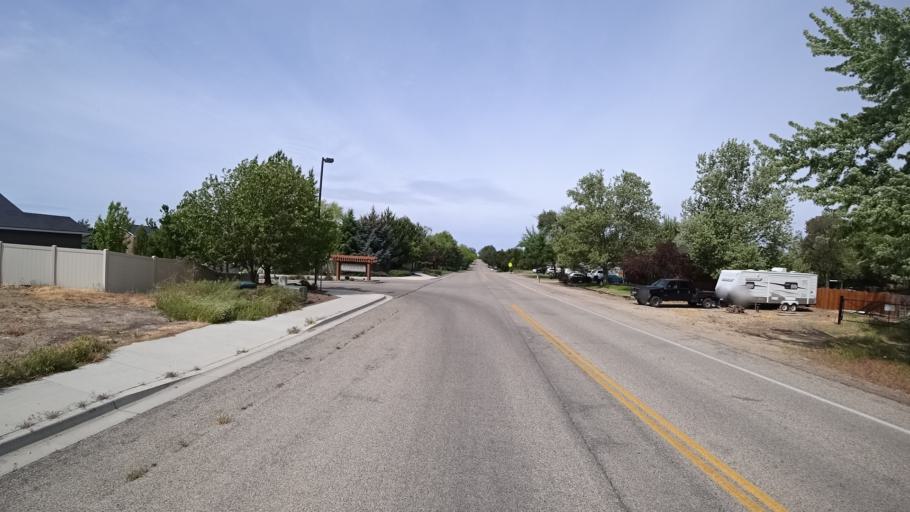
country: US
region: Idaho
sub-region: Ada County
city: Meridian
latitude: 43.5538
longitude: -116.3208
